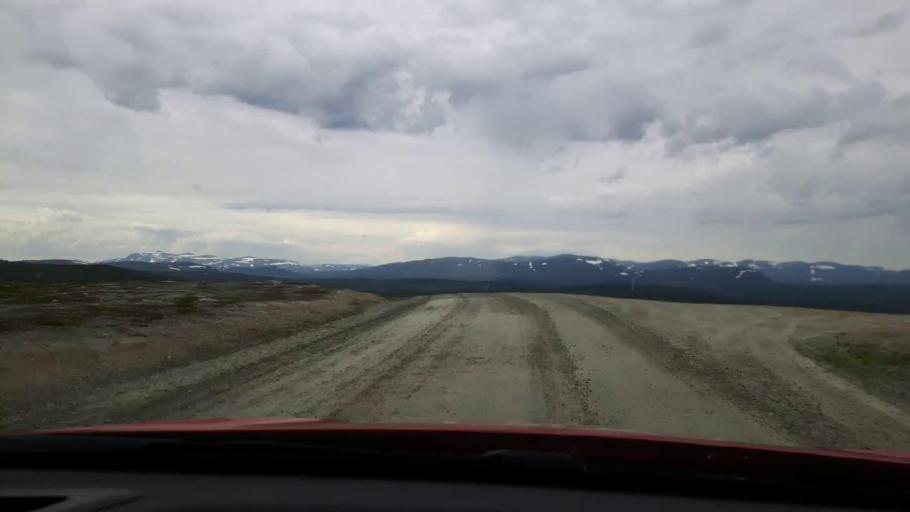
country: SE
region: Jaemtland
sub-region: Are Kommun
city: Are
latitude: 62.7696
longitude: 12.7669
